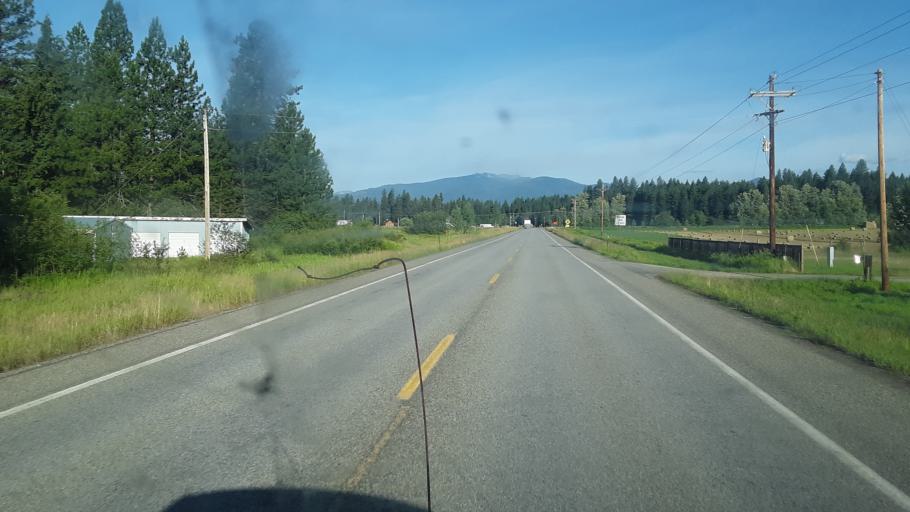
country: US
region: Idaho
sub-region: Boundary County
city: Bonners Ferry
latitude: 48.7303
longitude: -116.2369
